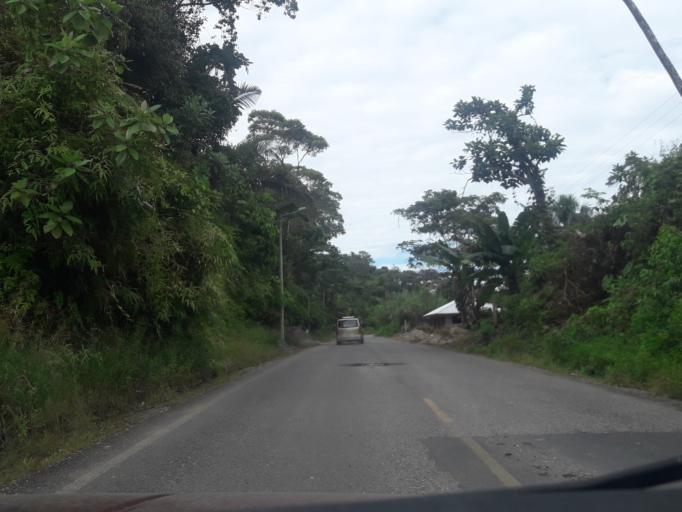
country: EC
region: Napo
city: Tena
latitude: -1.0314
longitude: -77.8881
